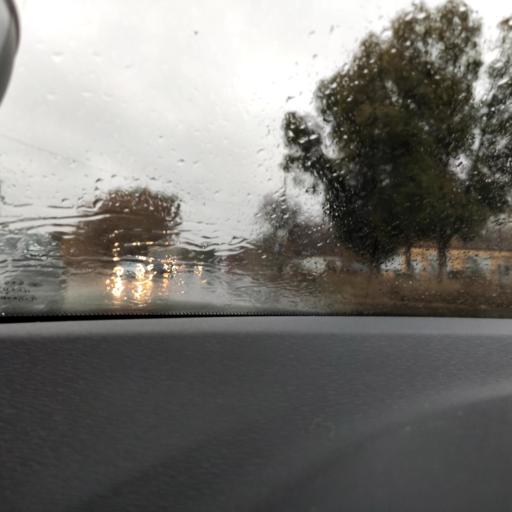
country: RU
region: Samara
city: Petra-Dubrava
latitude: 53.2440
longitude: 50.2711
